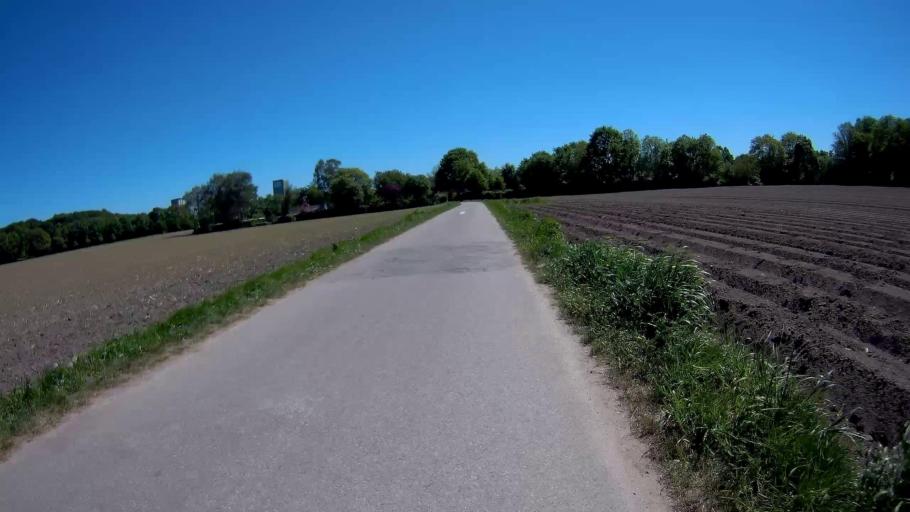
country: DE
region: North Rhine-Westphalia
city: Marl
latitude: 51.6049
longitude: 7.0629
